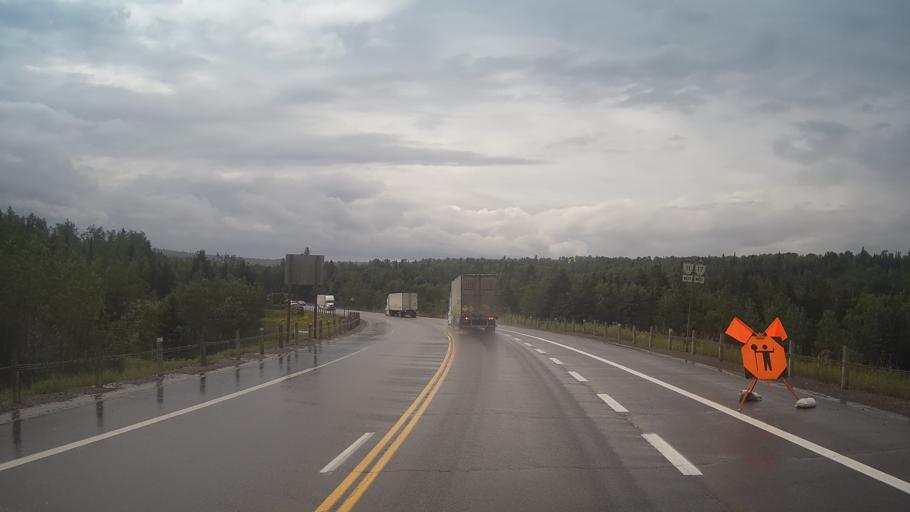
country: CA
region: Ontario
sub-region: Thunder Bay District
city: Thunder Bay
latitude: 48.5370
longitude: -89.6511
